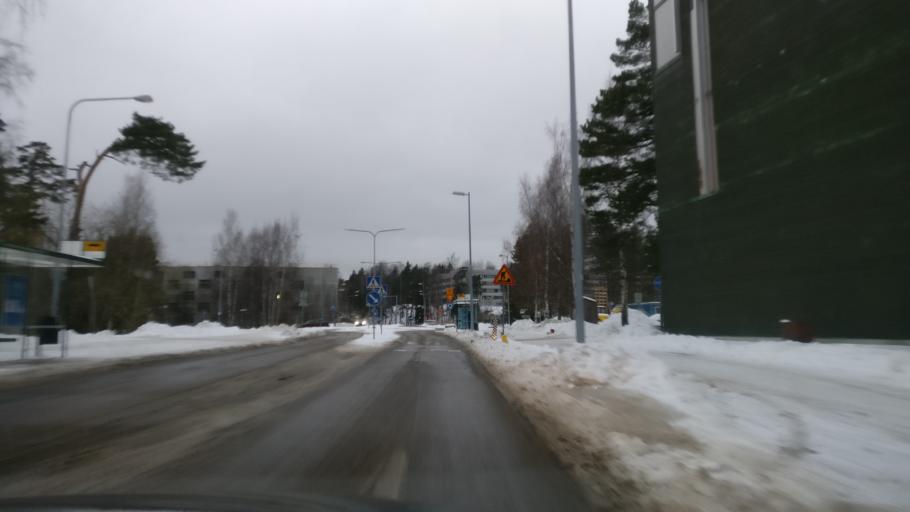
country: FI
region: Uusimaa
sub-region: Helsinki
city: Vantaa
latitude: 60.1782
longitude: 25.0536
